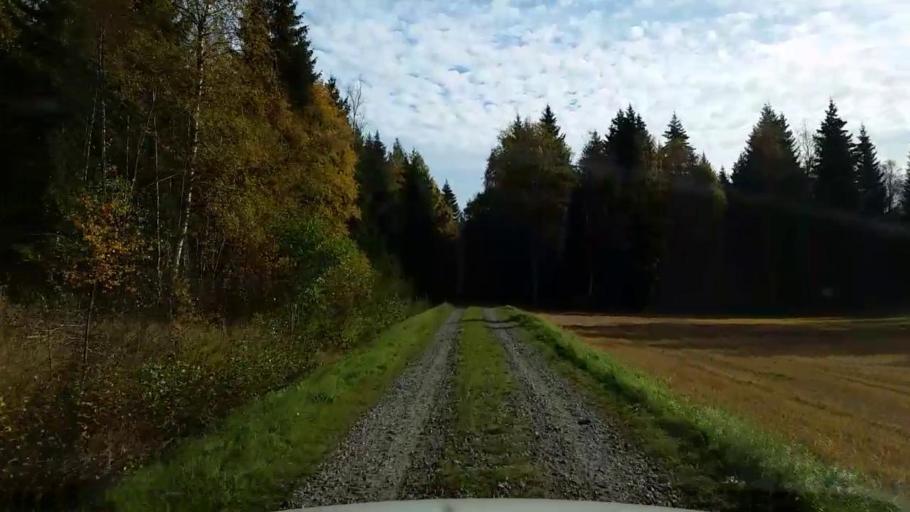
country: SE
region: Gaevleborg
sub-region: Ljusdals Kommun
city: Jaervsoe
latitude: 61.7818
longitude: 16.1737
